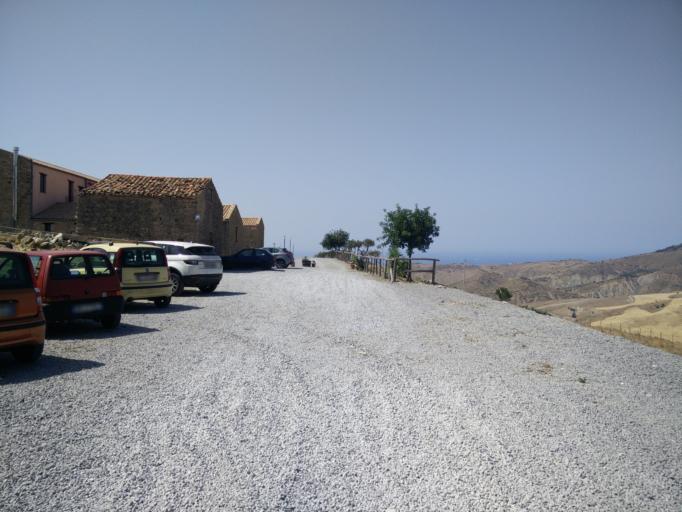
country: IT
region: Sicily
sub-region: Palermo
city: Cerda
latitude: 37.9277
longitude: 13.8741
